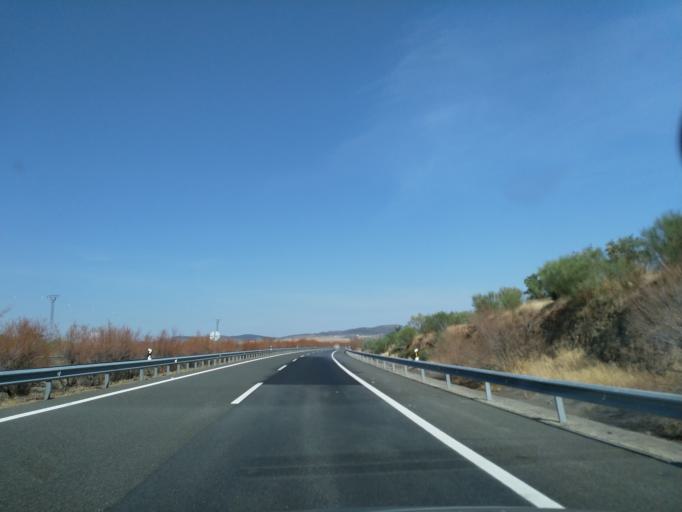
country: ES
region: Extremadura
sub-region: Provincia de Caceres
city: Aldea del Cano
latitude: 39.3463
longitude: -6.3425
